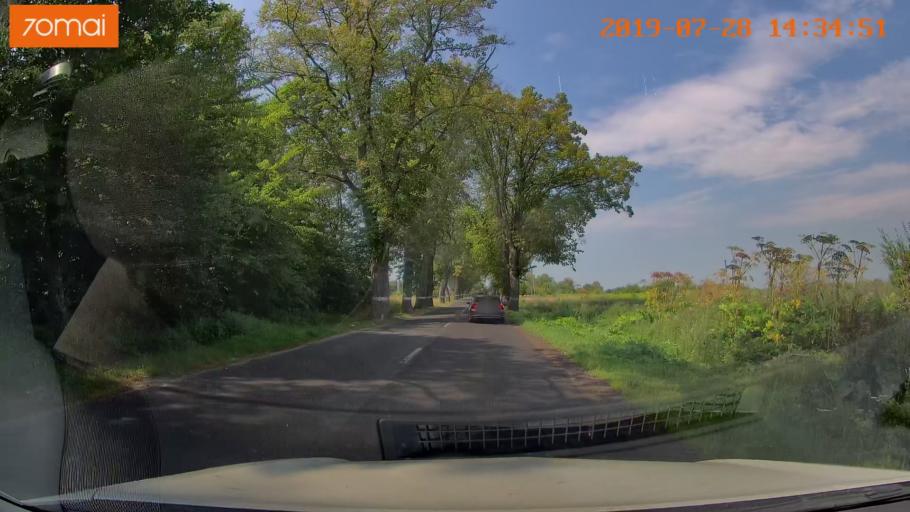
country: RU
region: Kaliningrad
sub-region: Gorod Kaliningrad
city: Yantarnyy
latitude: 54.8276
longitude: 20.0138
